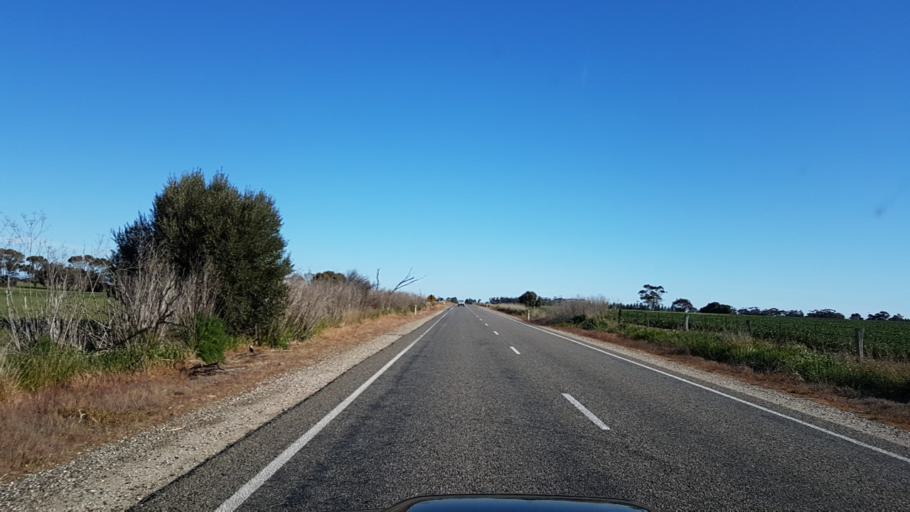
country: AU
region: South Australia
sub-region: Light
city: Kapunda
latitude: -34.2161
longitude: 138.7403
